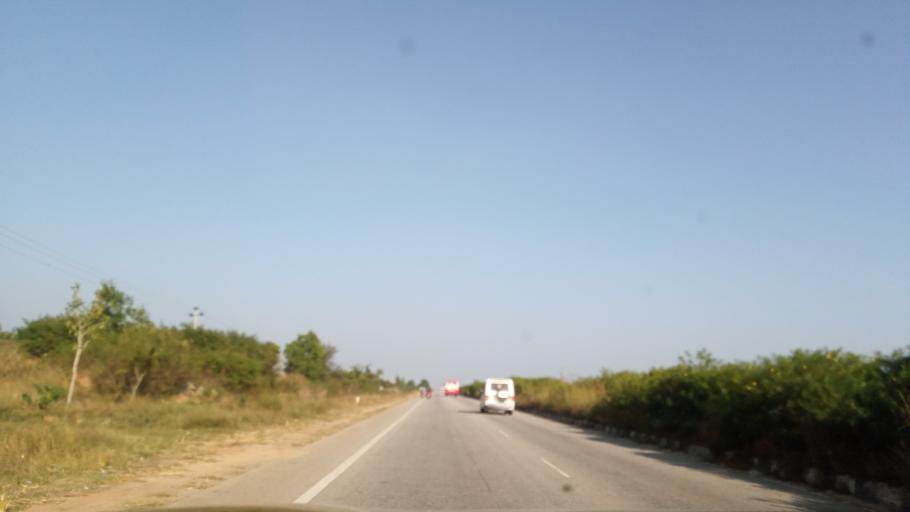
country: IN
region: Karnataka
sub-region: Kolar
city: Mulbagal
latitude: 13.1548
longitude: 78.3360
